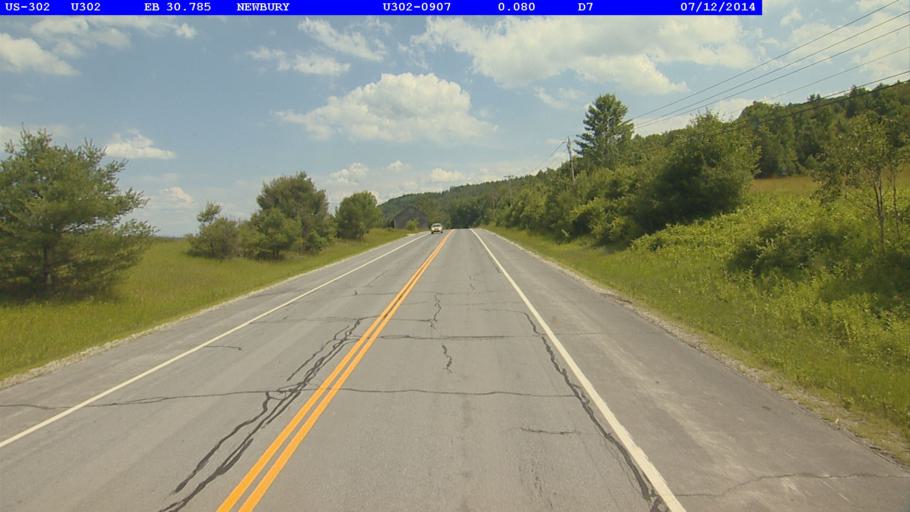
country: US
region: New Hampshire
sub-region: Grafton County
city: Woodsville
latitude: 44.1760
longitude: -72.1156
